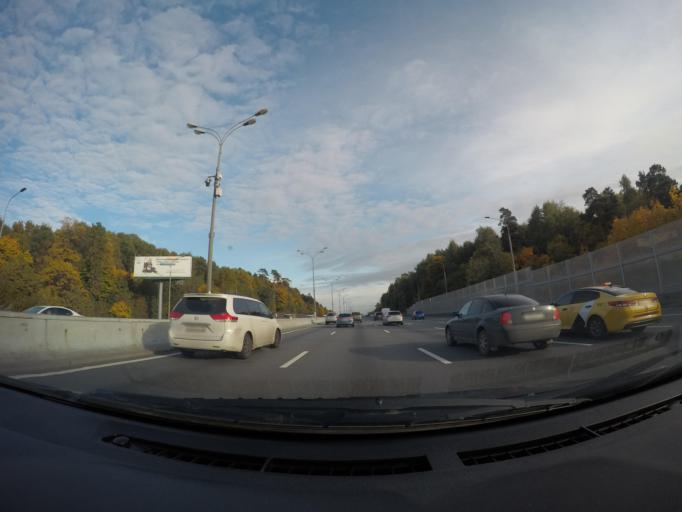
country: RU
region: Moscow
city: Yasenevo
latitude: 55.5869
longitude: 37.5482
